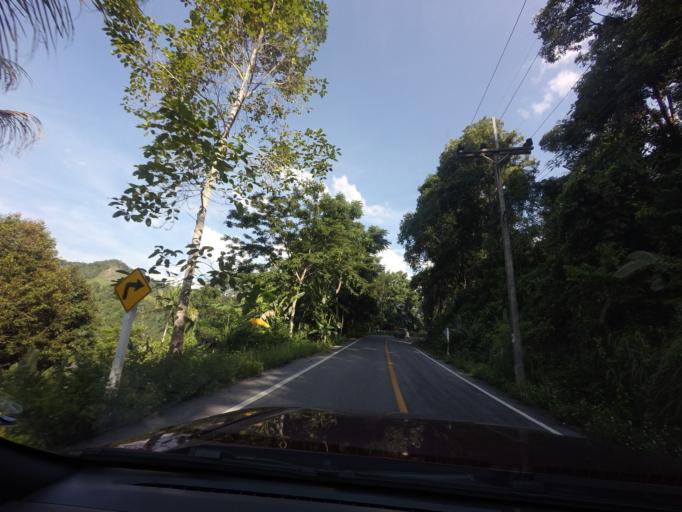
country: TH
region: Yala
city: Than To
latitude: 6.0733
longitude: 101.3366
